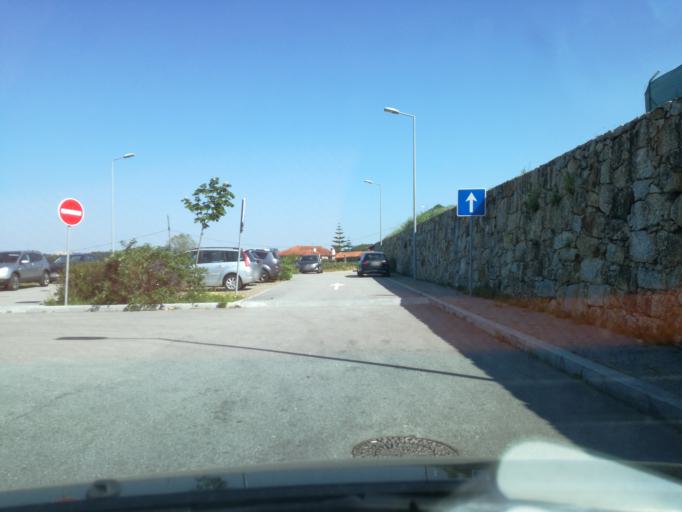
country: PT
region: Porto
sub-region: Maia
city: Maia
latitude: 41.2346
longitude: -8.6328
